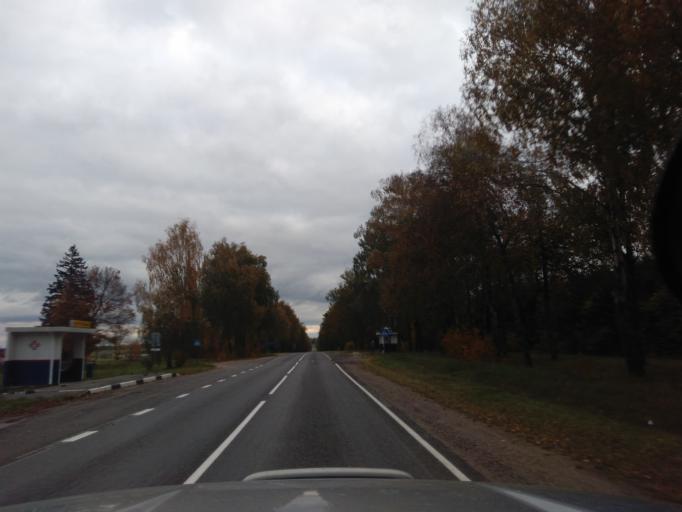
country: BY
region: Minsk
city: Slutsk
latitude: 53.2200
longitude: 27.4659
